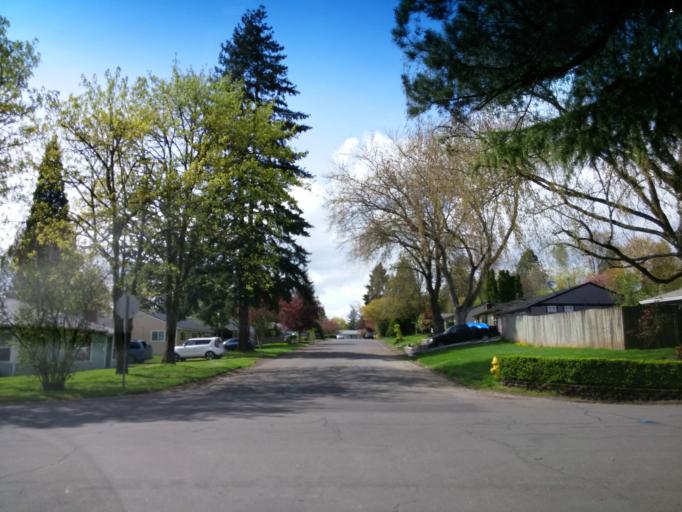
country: US
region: Oregon
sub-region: Washington County
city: Cedar Hills
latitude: 45.5035
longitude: -122.8086
